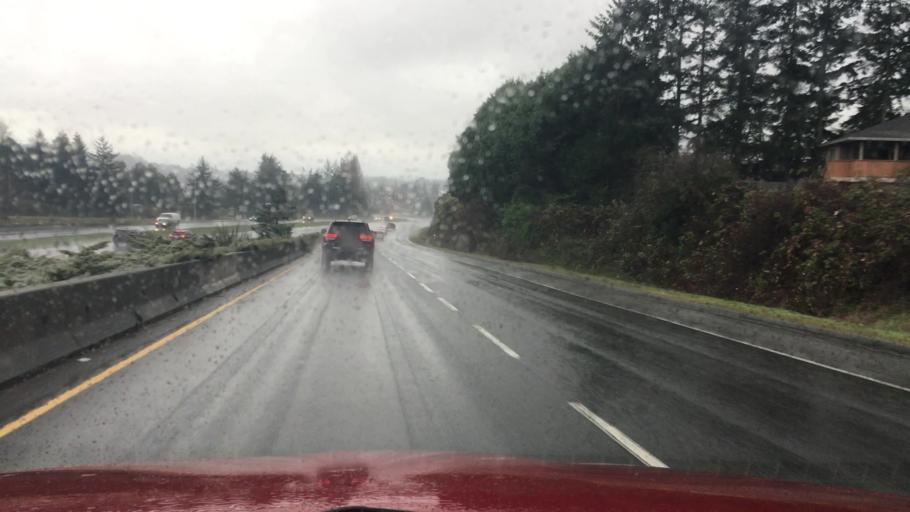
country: CA
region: British Columbia
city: Victoria
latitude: 48.4979
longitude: -123.3860
